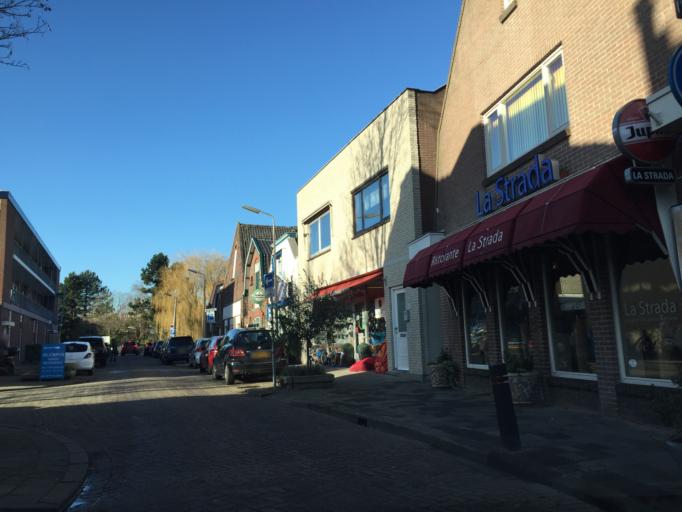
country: NL
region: South Holland
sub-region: Gemeente Lansingerland
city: Berkel en Rodenrijs
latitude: 51.9941
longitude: 4.4780
